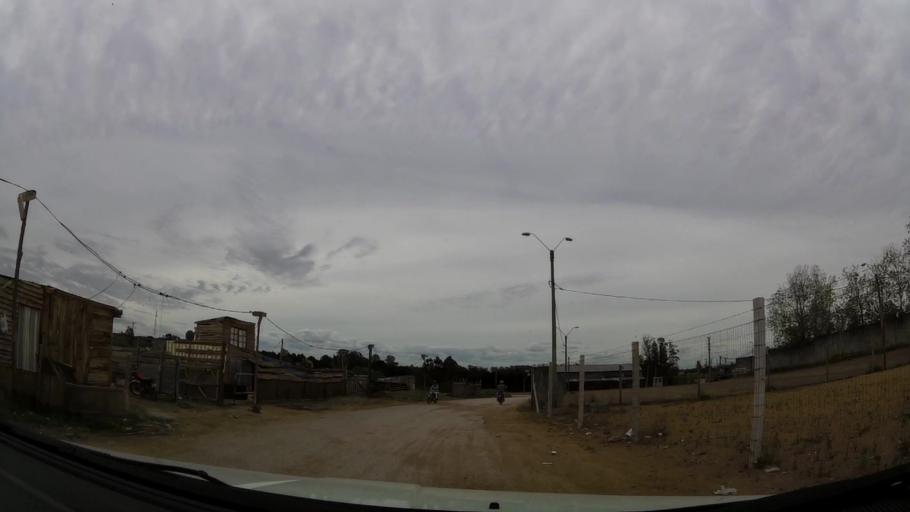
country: UY
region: Maldonado
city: Maldonado
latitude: -34.8831
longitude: -54.9552
